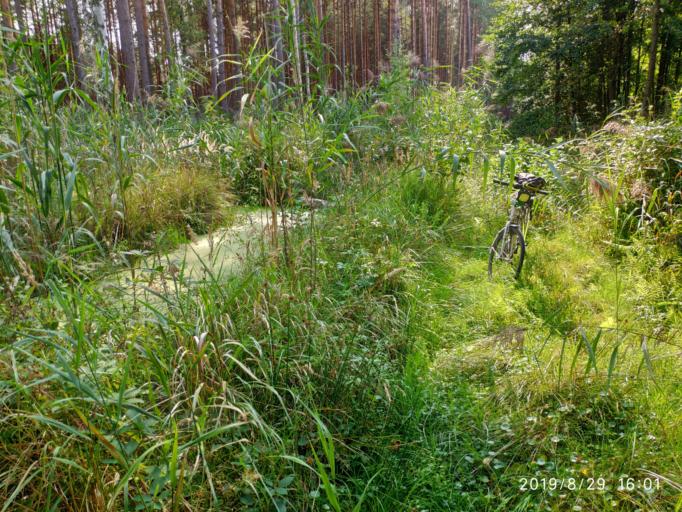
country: PL
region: Lubusz
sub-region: Powiat krosnienski
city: Bobrowice
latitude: 51.9809
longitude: 15.0301
